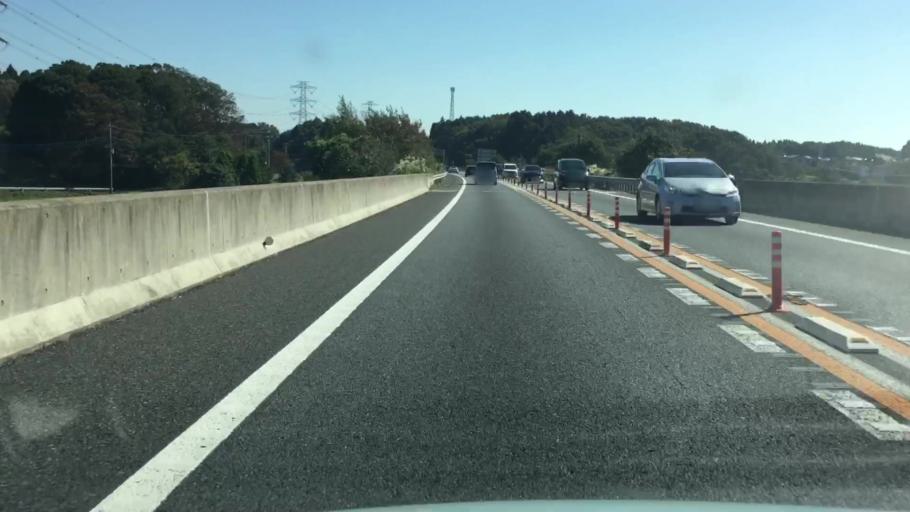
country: JP
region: Ibaraki
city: Ushiku
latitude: 35.9929
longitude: 140.1637
